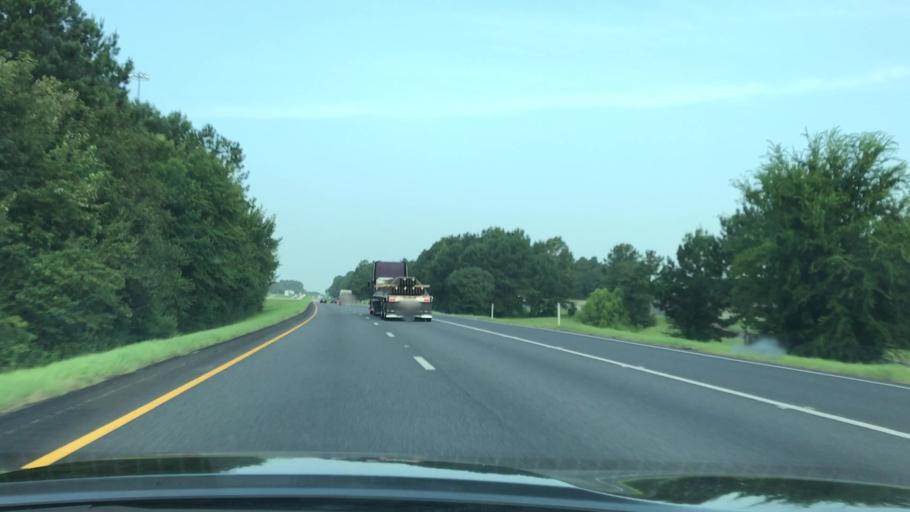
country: US
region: Texas
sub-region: Gregg County
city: Kilgore
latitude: 32.4352
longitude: -94.8311
